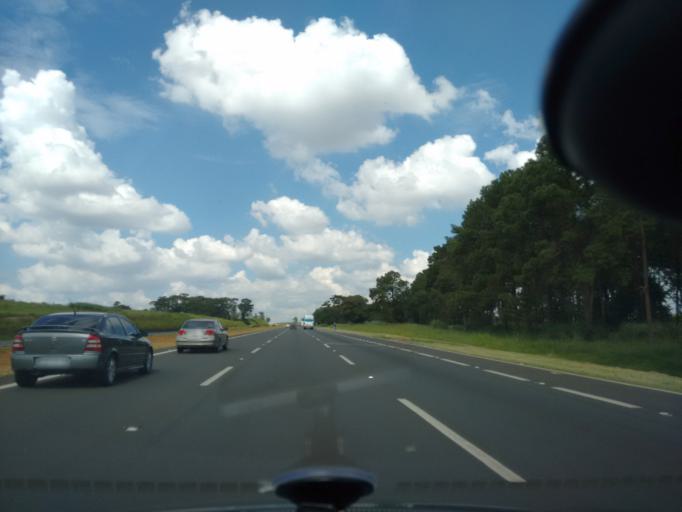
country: BR
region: Sao Paulo
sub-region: Hortolandia
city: Hortolandia
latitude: -22.9170
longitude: -47.1547
